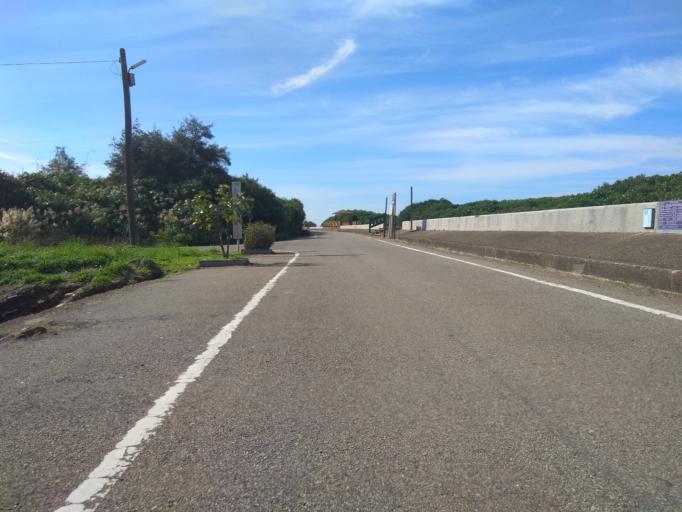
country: TW
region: Taiwan
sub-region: Hsinchu
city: Zhubei
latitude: 25.0152
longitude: 121.0338
